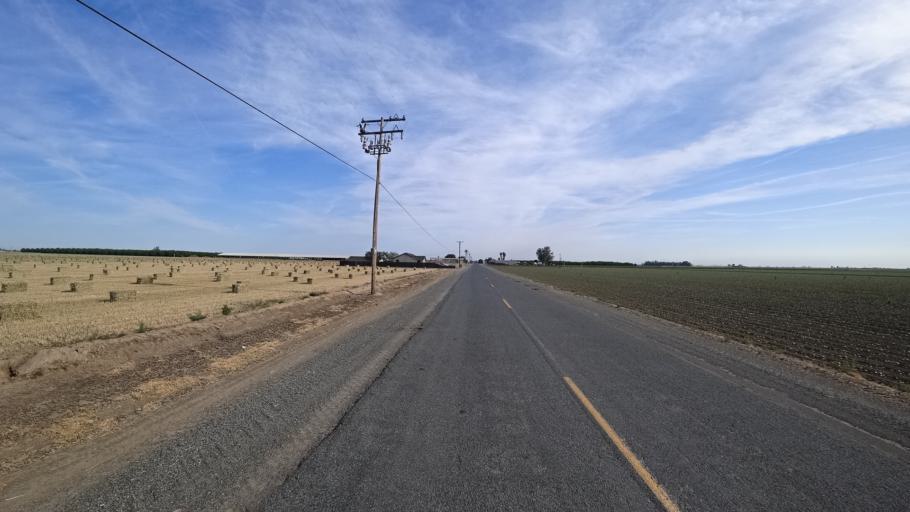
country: US
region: California
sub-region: Kings County
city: Hanford
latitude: 36.3609
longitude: -119.5471
